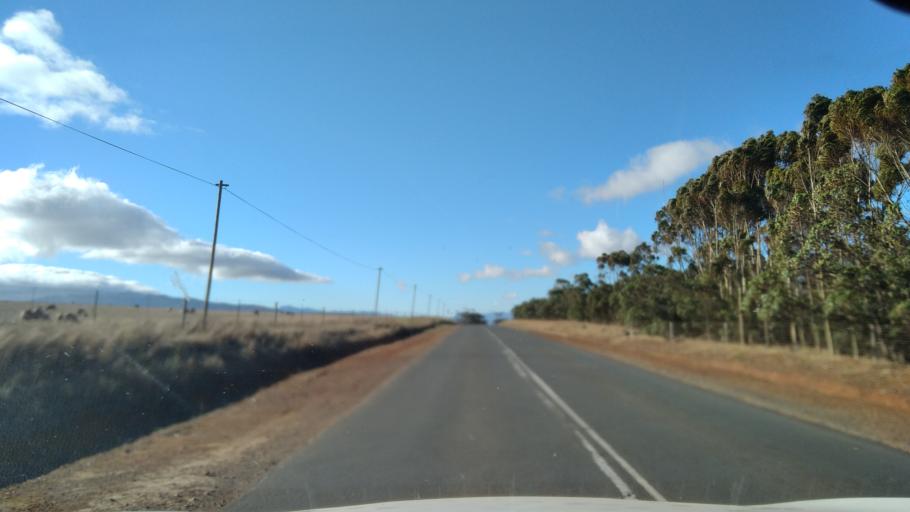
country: ZA
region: Western Cape
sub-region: Overberg District Municipality
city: Caledon
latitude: -34.2178
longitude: 19.2768
